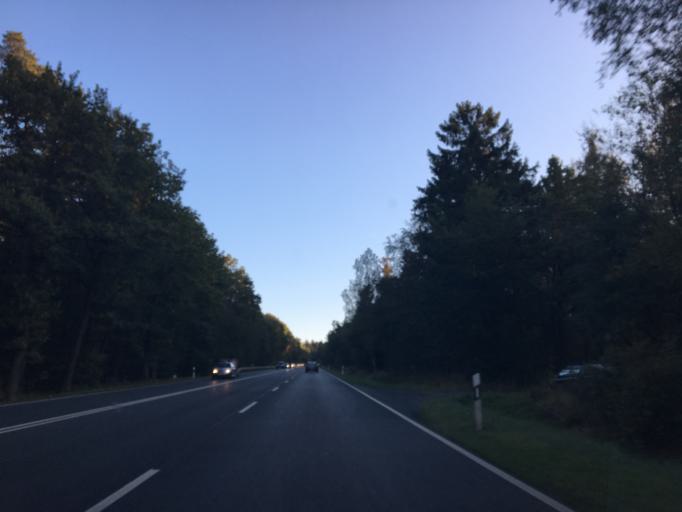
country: DE
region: Hesse
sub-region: Regierungsbezirk Darmstadt
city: Wehrheim
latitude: 50.2792
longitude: 8.5699
